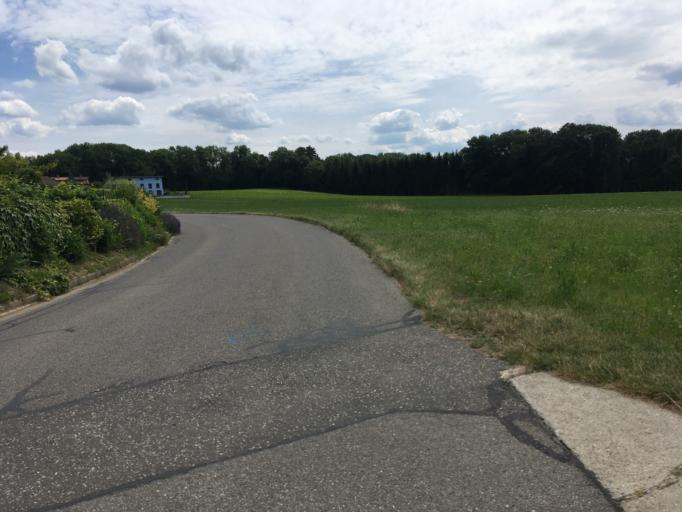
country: CH
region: Fribourg
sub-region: Broye District
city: Estavayer-le-Lac
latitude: 46.8701
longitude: 6.8810
